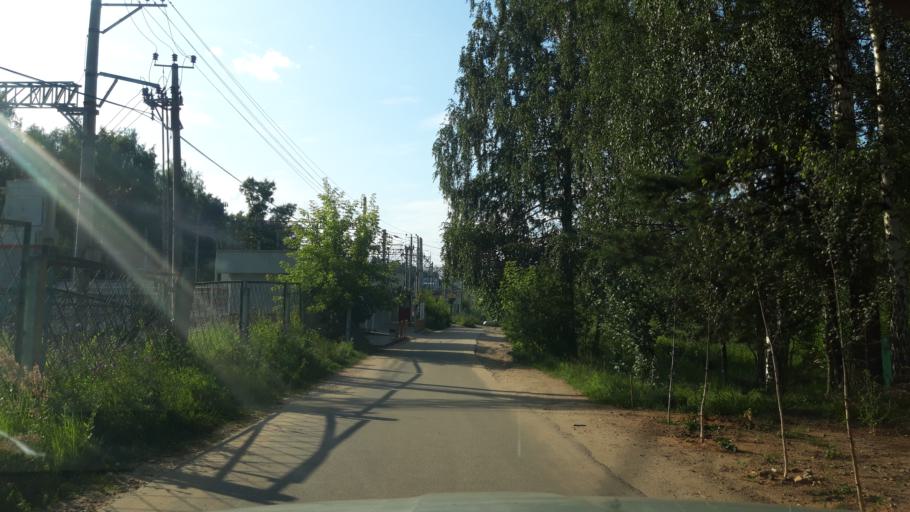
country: RU
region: Moskovskaya
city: Povarovo
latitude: 56.0643
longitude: 37.0767
